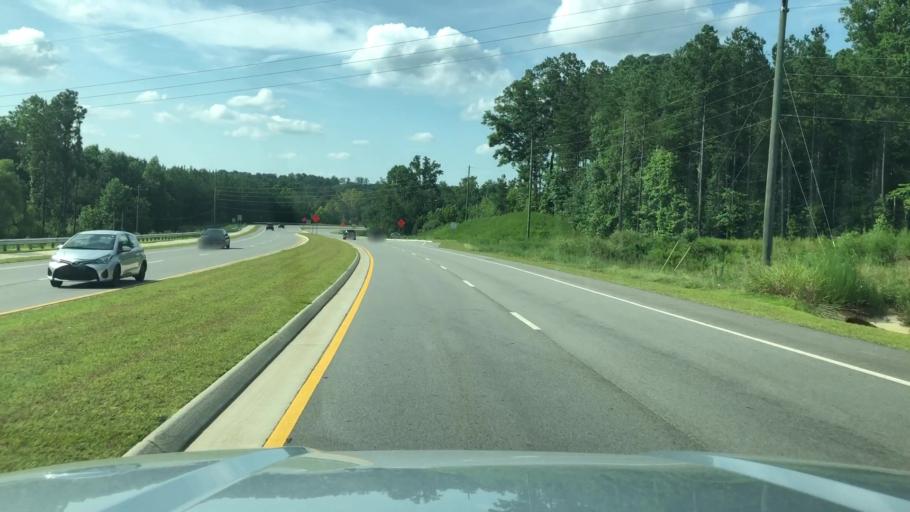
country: US
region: Georgia
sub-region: Paulding County
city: Hiram
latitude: 33.8761
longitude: -84.7810
